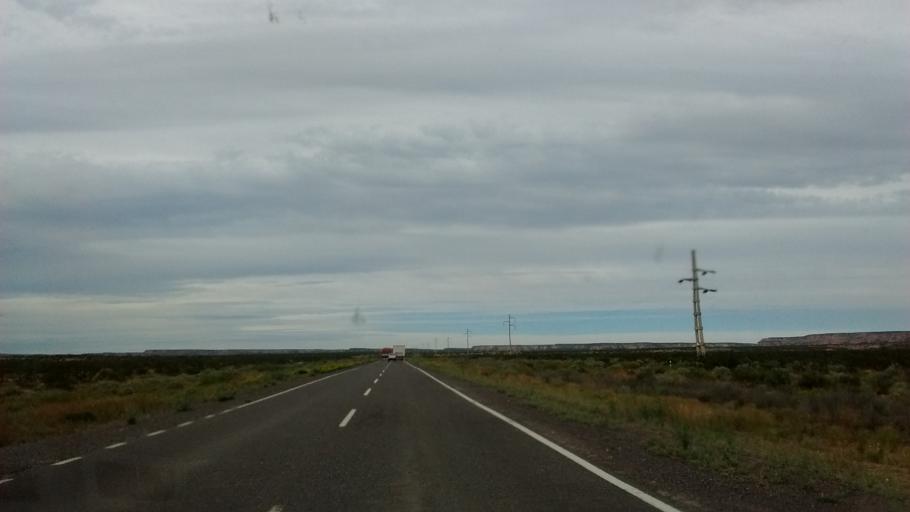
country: AR
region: Rio Negro
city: Catriel
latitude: -38.1344
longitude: -67.9362
